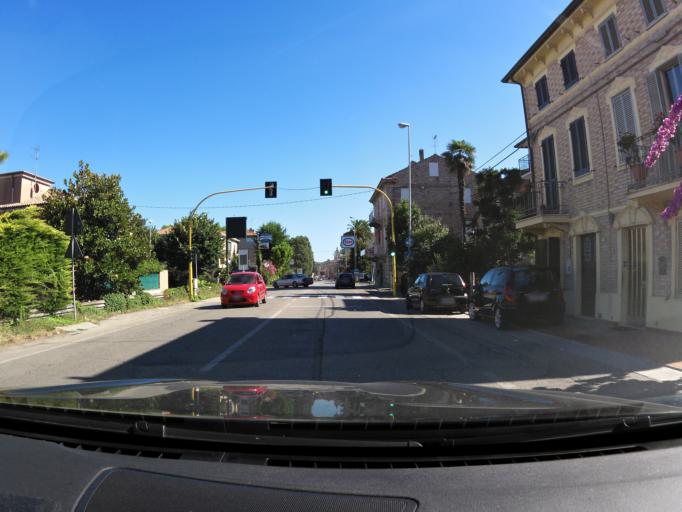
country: IT
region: The Marches
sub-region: Province of Fermo
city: Porto San Giorgio
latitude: 43.1857
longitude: 13.7912
